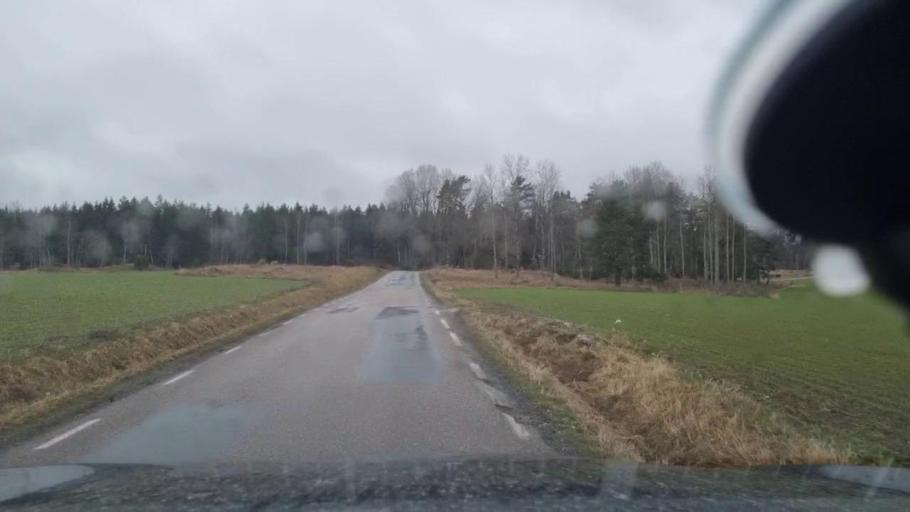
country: SE
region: Stockholm
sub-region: Vallentuna Kommun
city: Vallentuna
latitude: 59.4960
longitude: 18.0057
